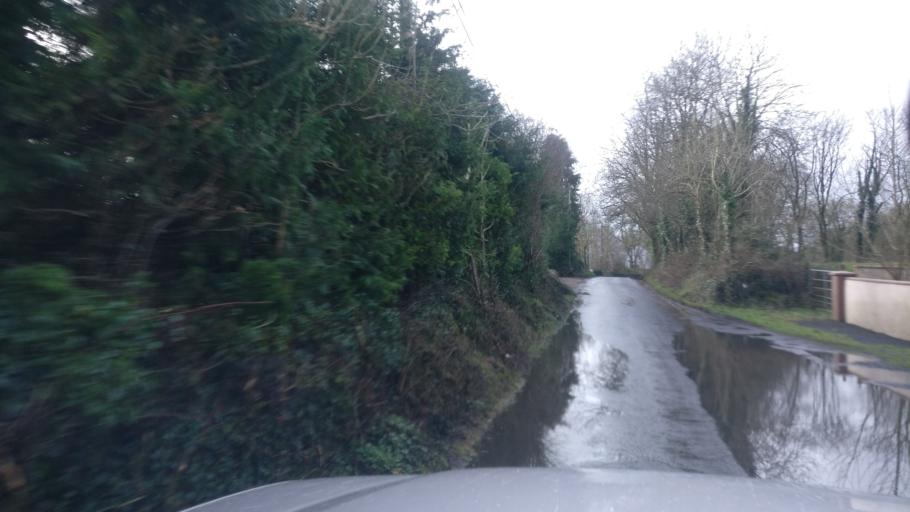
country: IE
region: Connaught
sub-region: County Galway
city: Athenry
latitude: 53.2738
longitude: -8.7688
